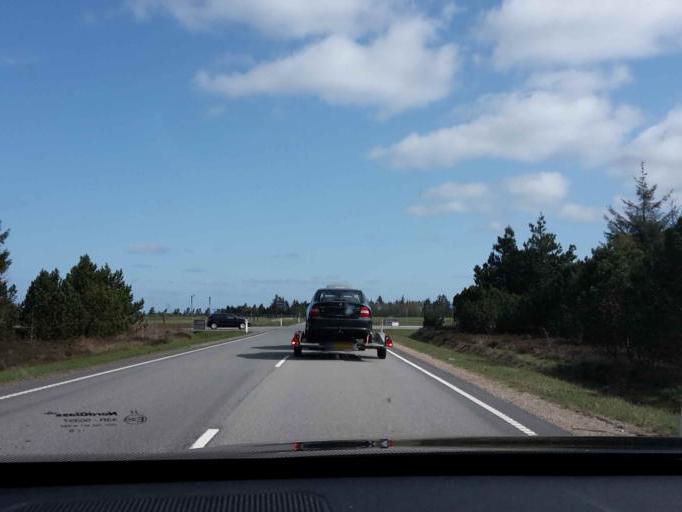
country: DK
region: South Denmark
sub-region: Billund Kommune
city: Grindsted
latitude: 55.6764
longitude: 8.9585
